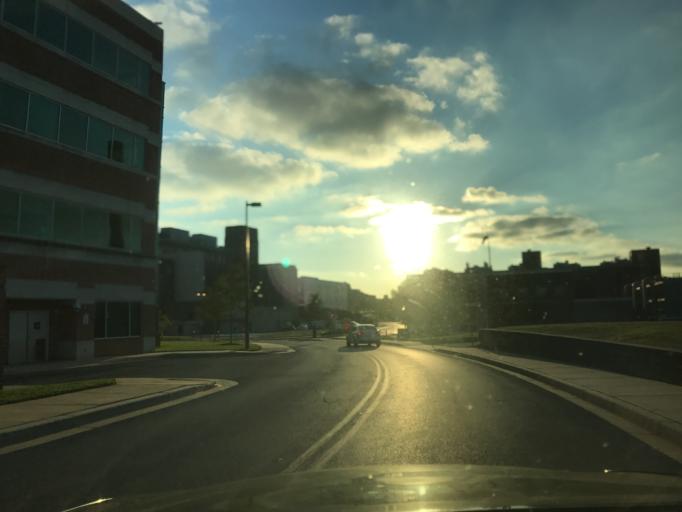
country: US
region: Maryland
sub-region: Baltimore County
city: Rosedale
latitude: 39.2920
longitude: -76.5453
